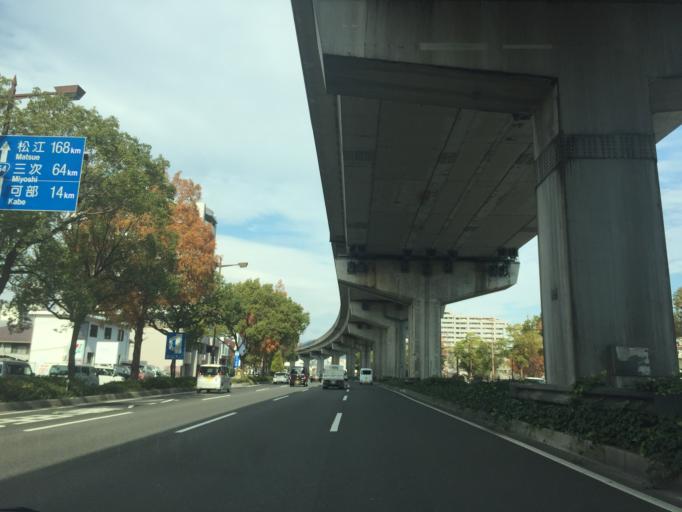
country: JP
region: Hiroshima
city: Hiroshima-shi
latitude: 34.4176
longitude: 132.4648
